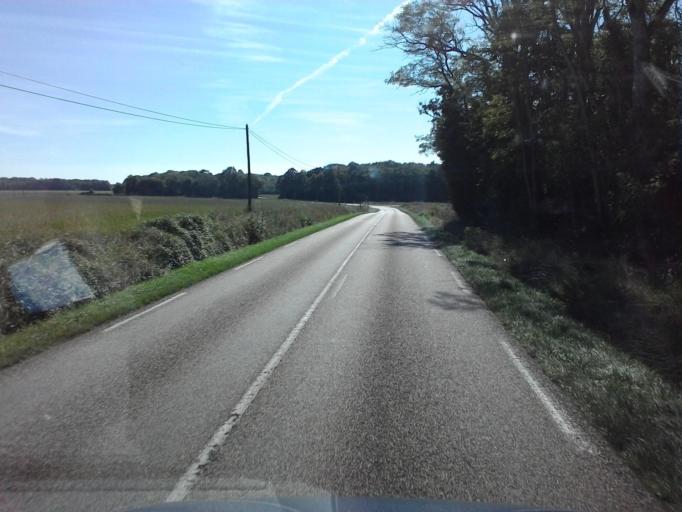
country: FR
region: Bourgogne
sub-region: Departement de l'Yonne
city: Joux-la-Ville
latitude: 47.5973
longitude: 3.8648
